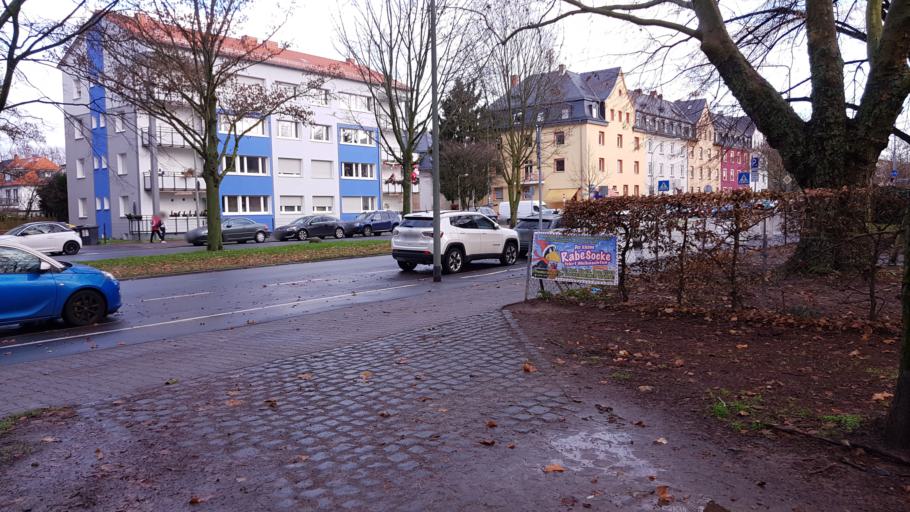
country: DE
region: Hesse
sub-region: Regierungsbezirk Darmstadt
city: Frankfurt am Main
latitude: 50.1455
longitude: 8.6573
